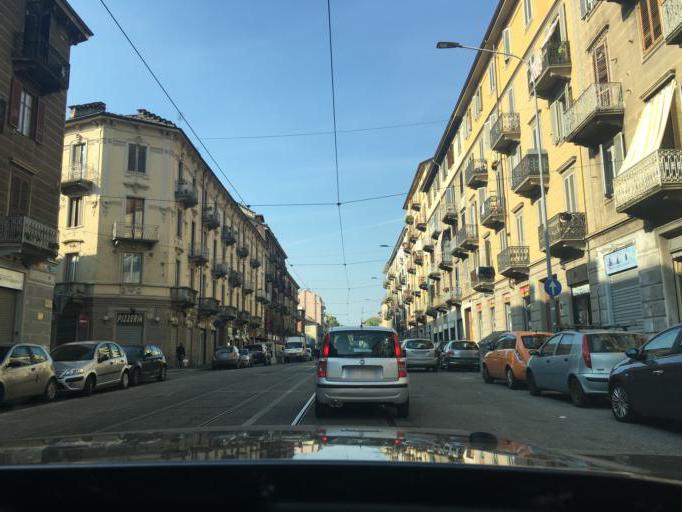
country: IT
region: Piedmont
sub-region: Provincia di Torino
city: Turin
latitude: 45.0879
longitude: 7.6932
